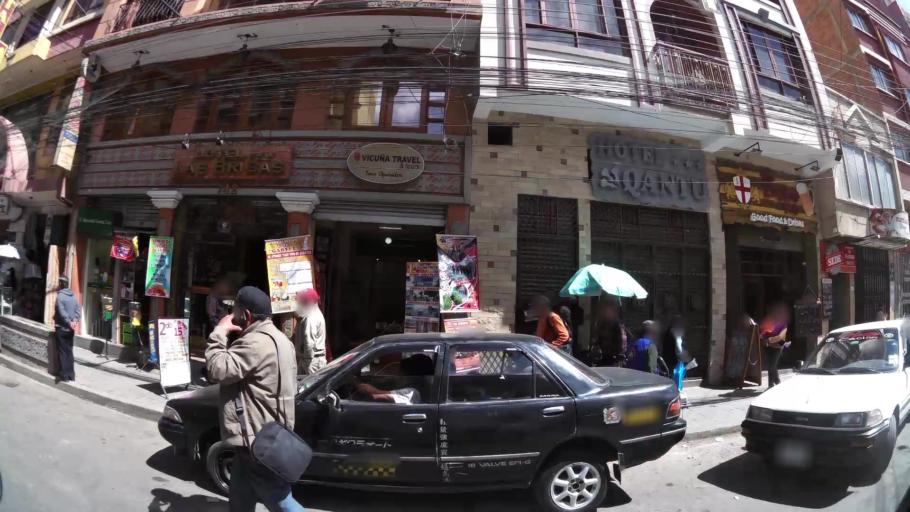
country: BO
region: La Paz
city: La Paz
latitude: -16.4961
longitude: -68.1400
